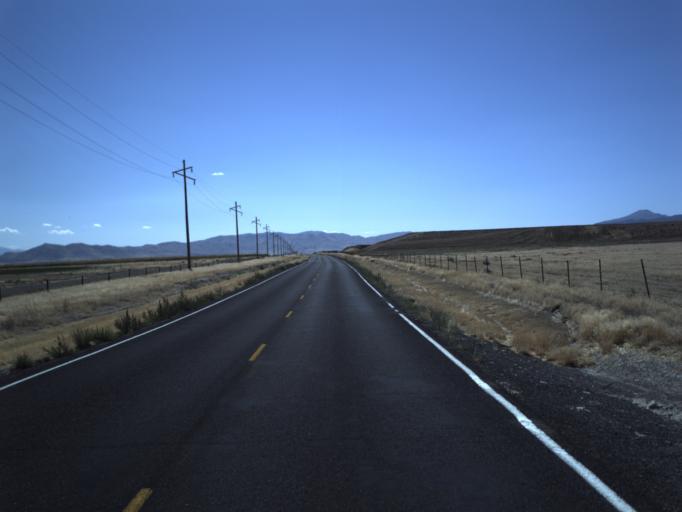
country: US
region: Utah
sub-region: Utah County
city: Genola
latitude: 40.0452
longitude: -111.9583
